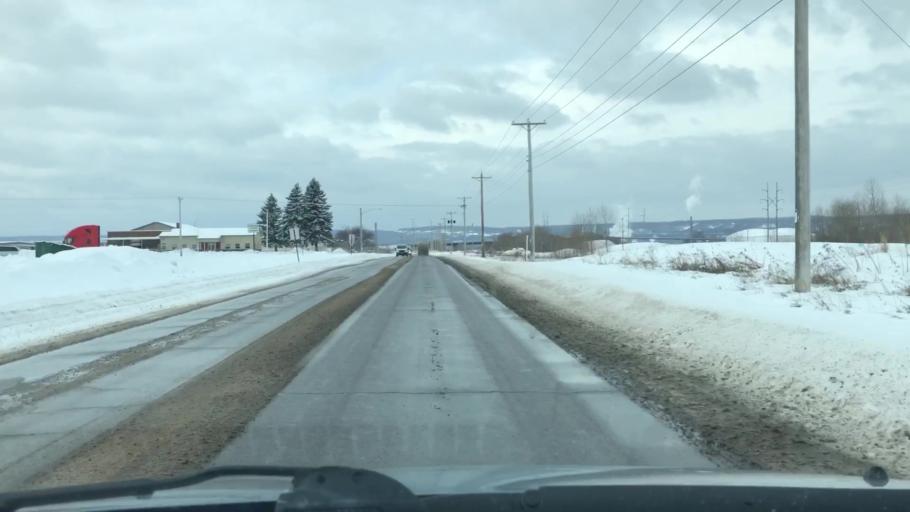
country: US
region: Wisconsin
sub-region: Douglas County
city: Superior
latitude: 46.7280
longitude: -92.1188
